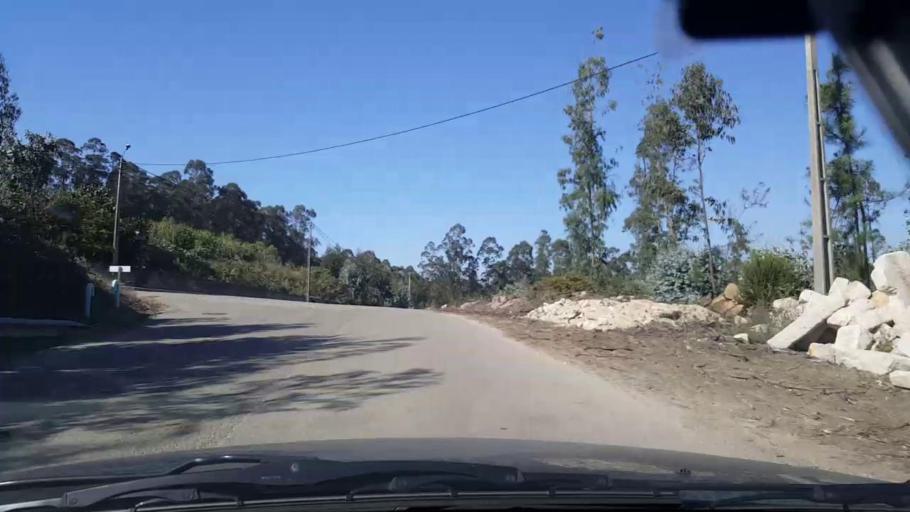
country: PT
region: Braga
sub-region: Vila Nova de Famalicao
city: Ribeirao
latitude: 41.3820
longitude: -8.6402
